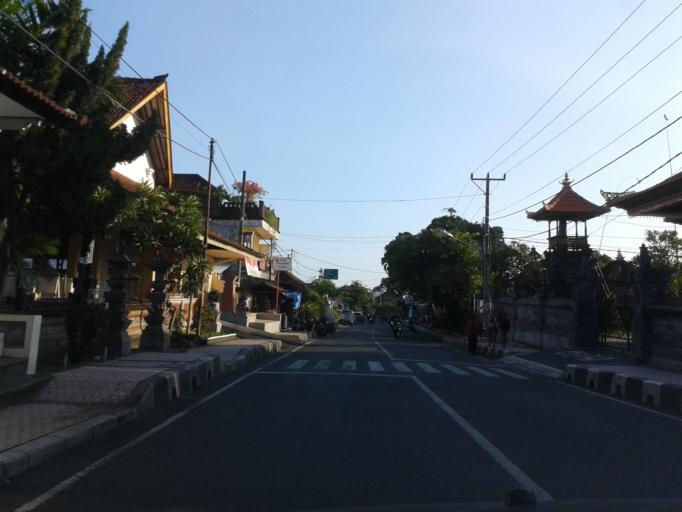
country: ID
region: Bali
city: Semarapura
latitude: -8.5384
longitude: 115.4033
